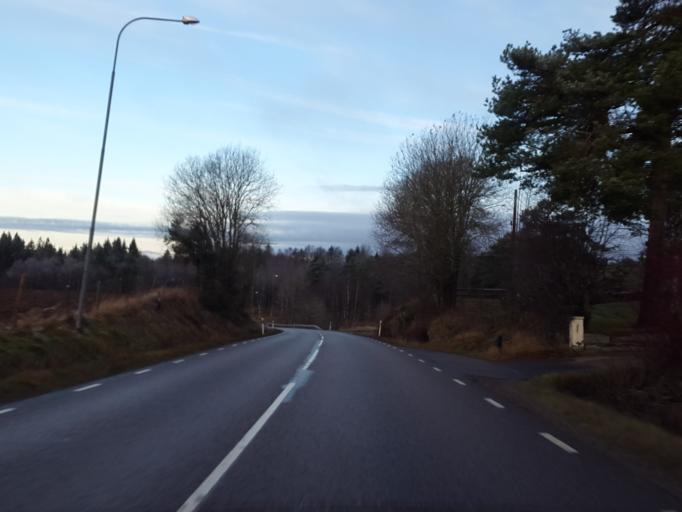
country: SE
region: Vaestra Goetaland
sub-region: Boras Kommun
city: Sjomarken
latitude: 57.7718
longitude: 12.8157
